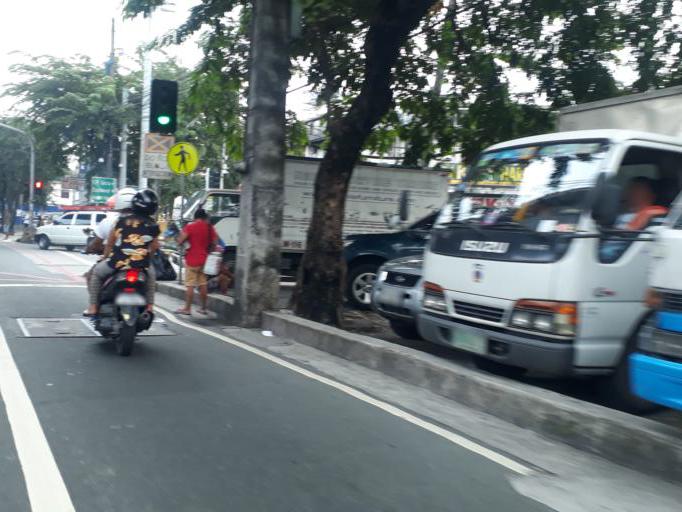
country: PH
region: Metro Manila
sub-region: Marikina
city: Calumpang
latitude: 14.6282
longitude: 121.0662
